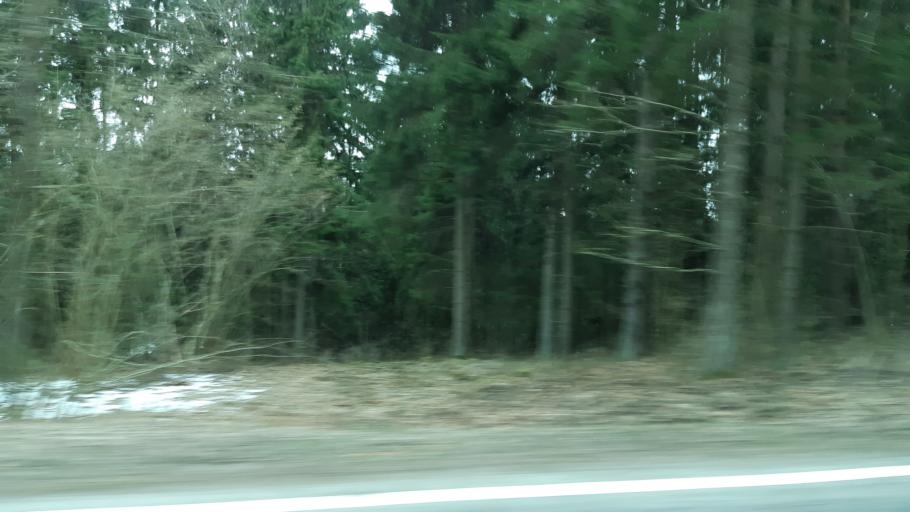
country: PL
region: Podlasie
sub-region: Suwalki
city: Suwalki
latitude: 54.3005
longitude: 22.9566
